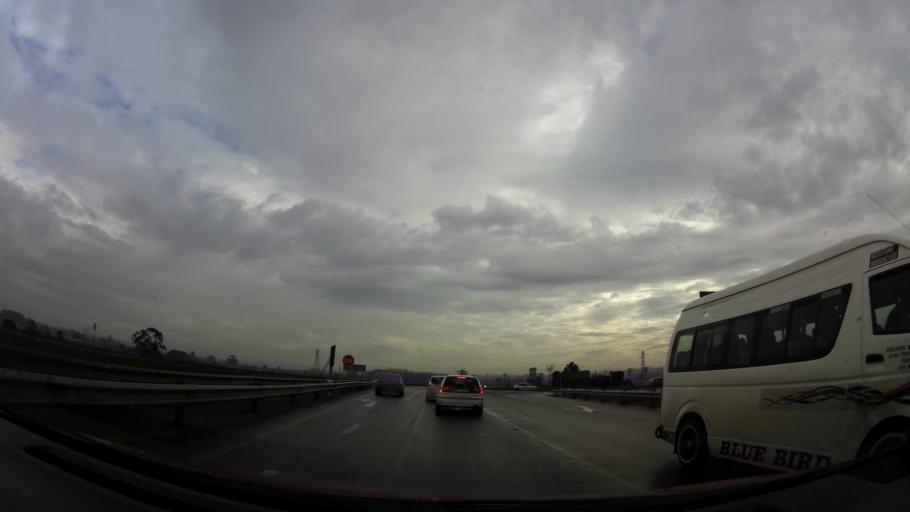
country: ZA
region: Gauteng
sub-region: City of Johannesburg Metropolitan Municipality
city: Soweto
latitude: -26.2963
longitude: 27.8469
